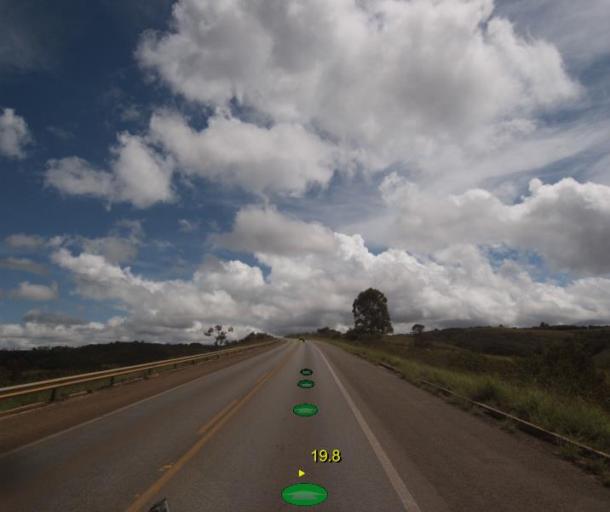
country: BR
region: Federal District
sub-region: Brasilia
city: Brasilia
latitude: -15.7427
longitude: -48.3732
